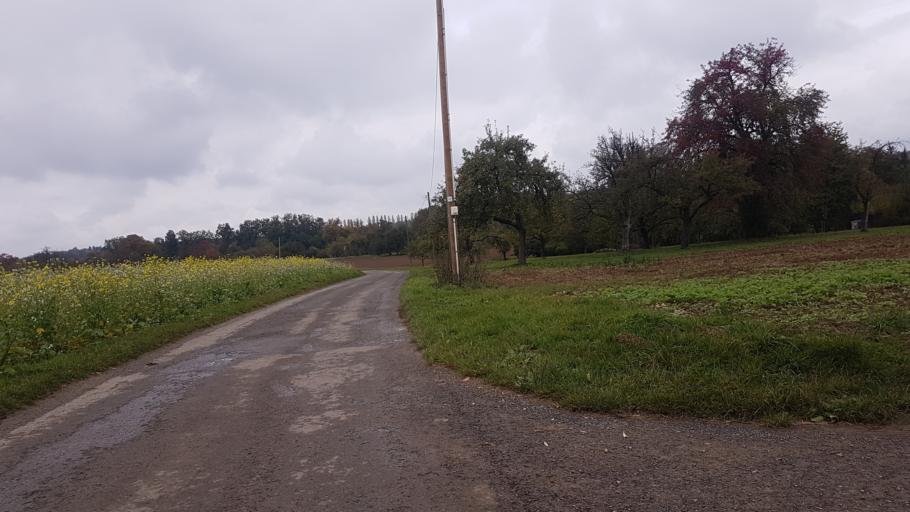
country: DE
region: Baden-Wuerttemberg
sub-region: Tuebingen Region
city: Dusslingen
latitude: 48.4616
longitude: 9.0443
